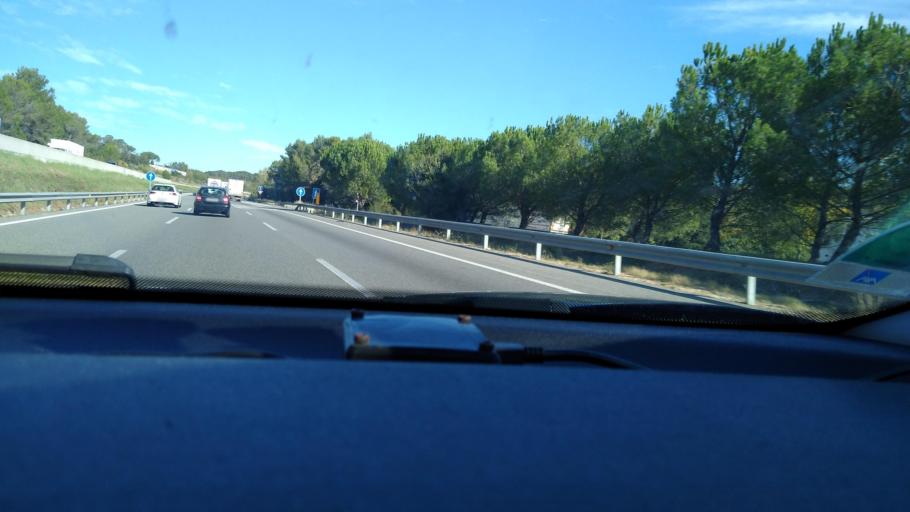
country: ES
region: Catalonia
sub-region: Provincia de Girona
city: Cervia de Ter
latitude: 42.0804
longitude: 2.8899
